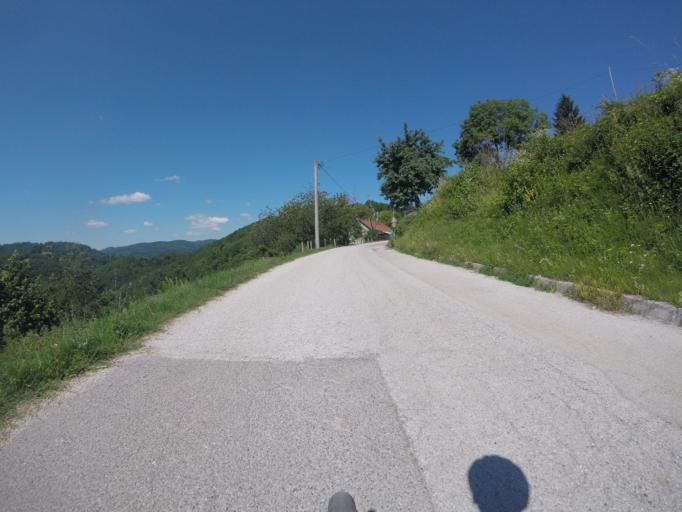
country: SI
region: Kostanjevica na Krki
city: Kostanjevica na Krki
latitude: 45.8101
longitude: 15.5069
